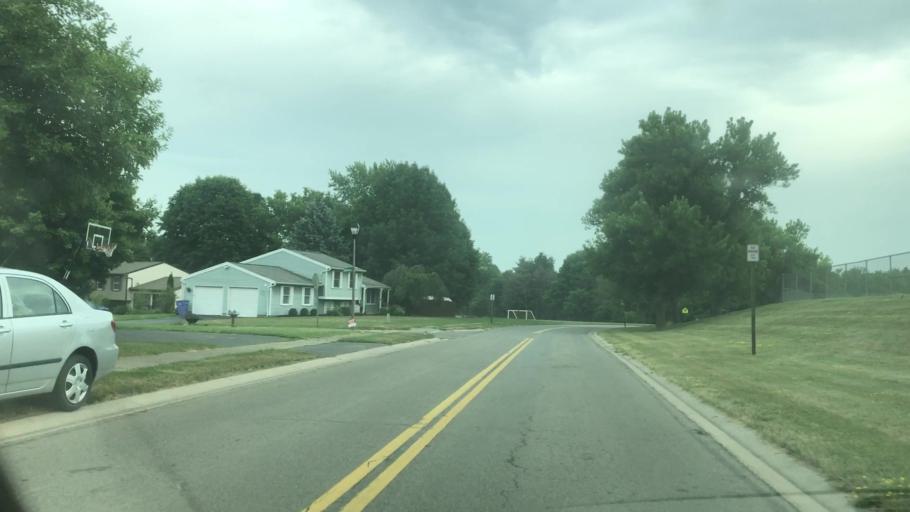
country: US
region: New York
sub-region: Wayne County
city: Macedon
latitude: 43.1268
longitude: -77.3069
